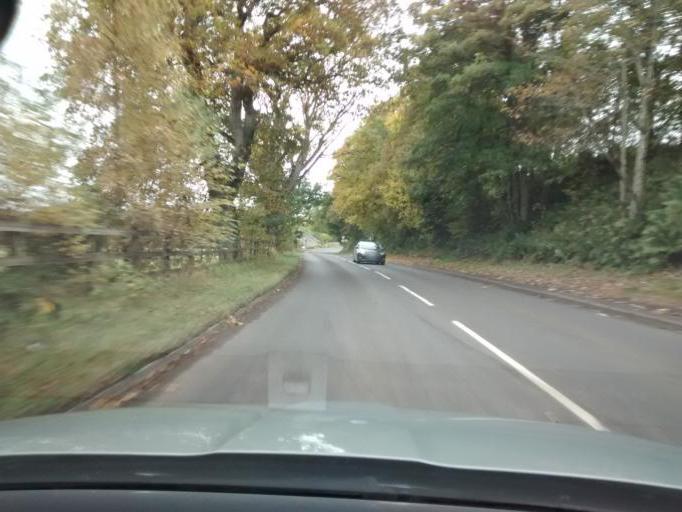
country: GB
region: Scotland
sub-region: Perth and Kinross
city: Luncarty
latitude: 56.4588
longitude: -3.4727
